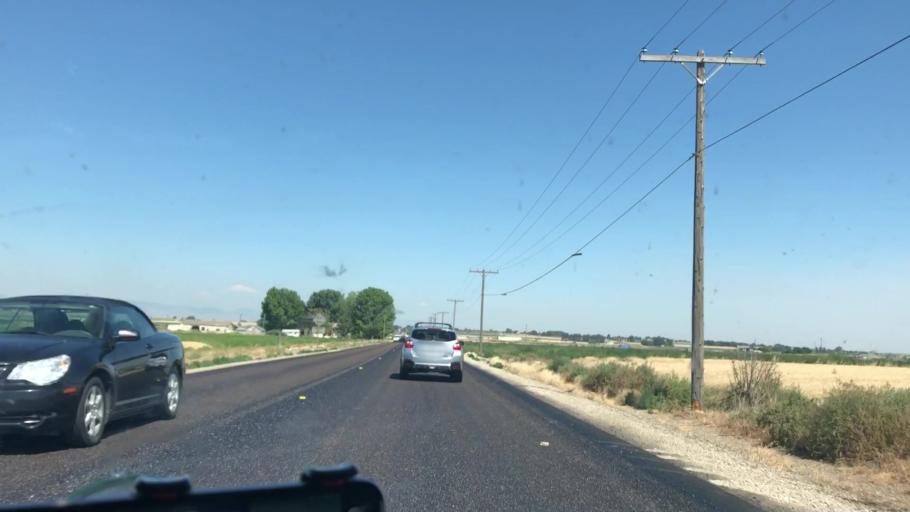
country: US
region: Idaho
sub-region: Owyhee County
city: Marsing
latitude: 43.6031
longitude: -116.7685
